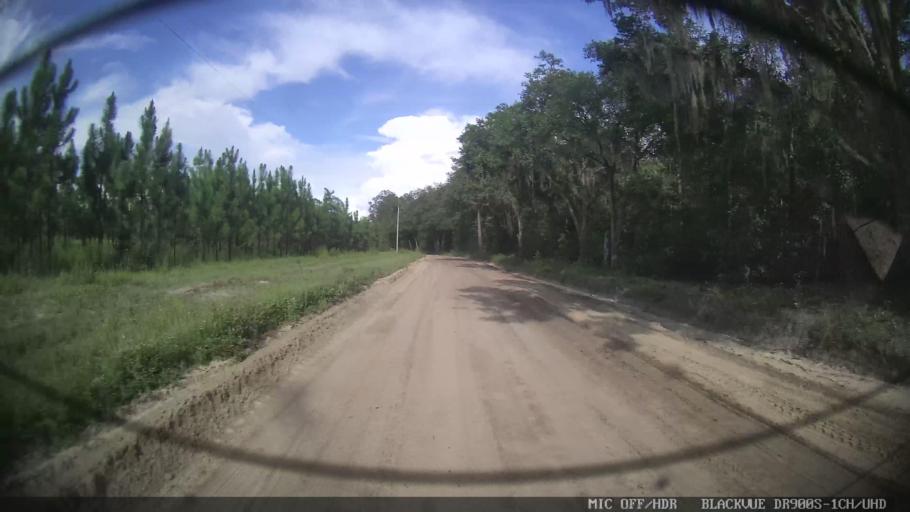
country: US
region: Georgia
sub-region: Echols County
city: Statenville
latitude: 30.6192
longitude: -83.2181
